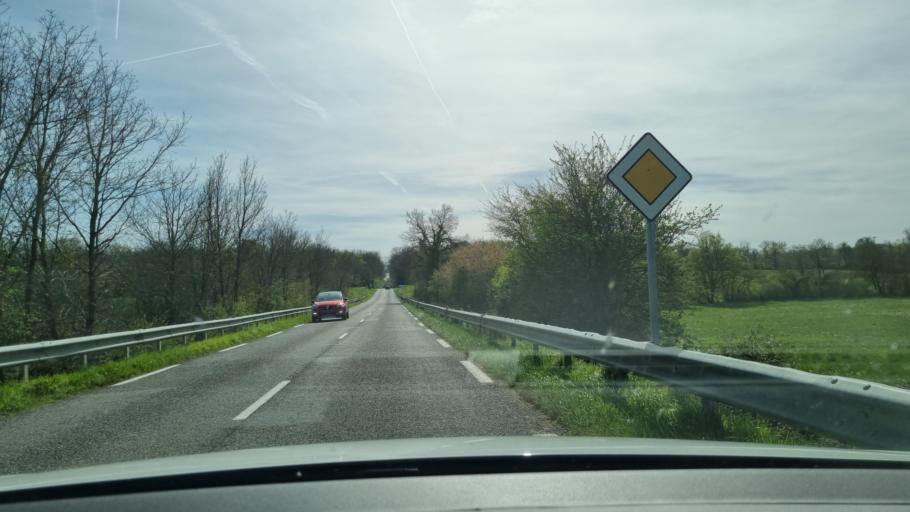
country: FR
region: Midi-Pyrenees
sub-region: Departement du Gers
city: Lombez
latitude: 43.4204
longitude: 0.8131
